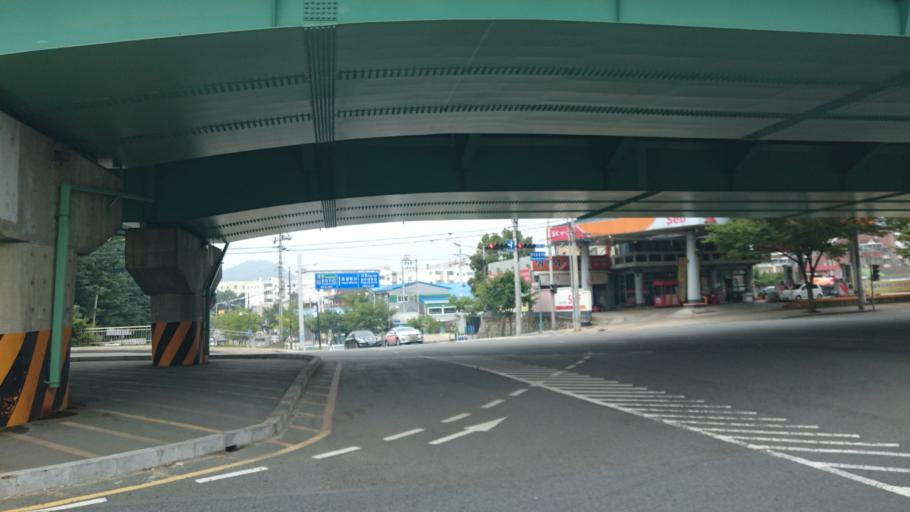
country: KR
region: Daegu
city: Daegu
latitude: 35.8785
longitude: 128.6497
